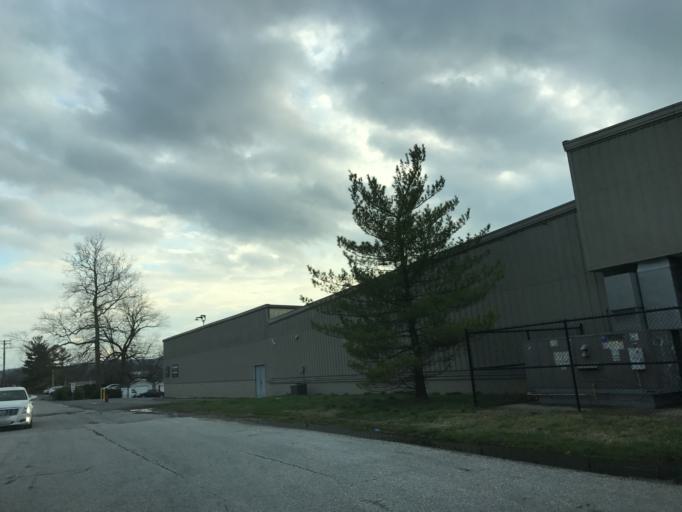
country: US
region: Maryland
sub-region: Baltimore County
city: Cockeysville
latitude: 39.4839
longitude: -76.6454
